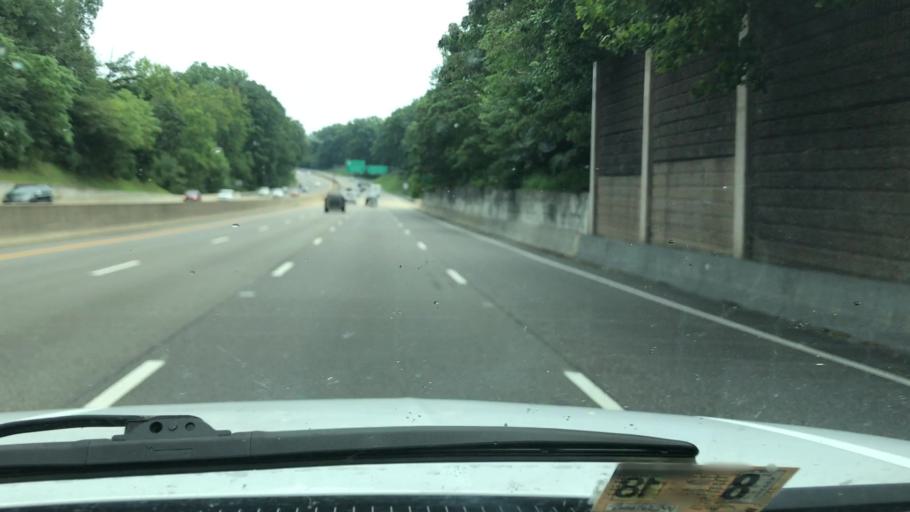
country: US
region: Virginia
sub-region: Chesterfield County
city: Bensley
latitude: 37.4588
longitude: -77.4962
